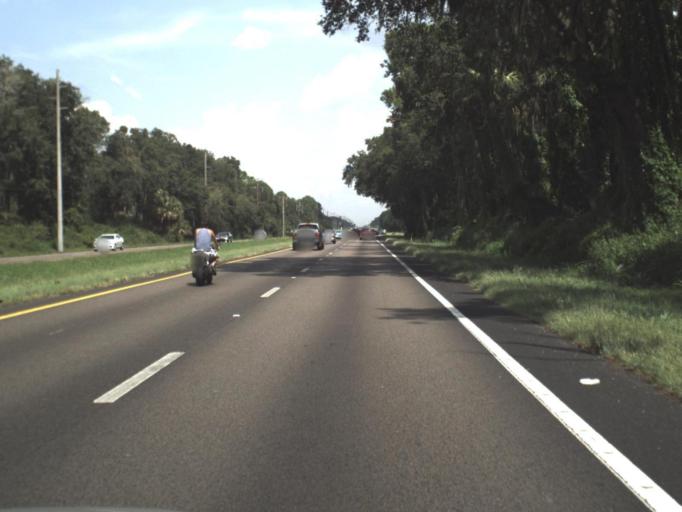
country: US
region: Florida
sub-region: Hillsborough County
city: Valrico
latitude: 27.9377
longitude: -82.1982
